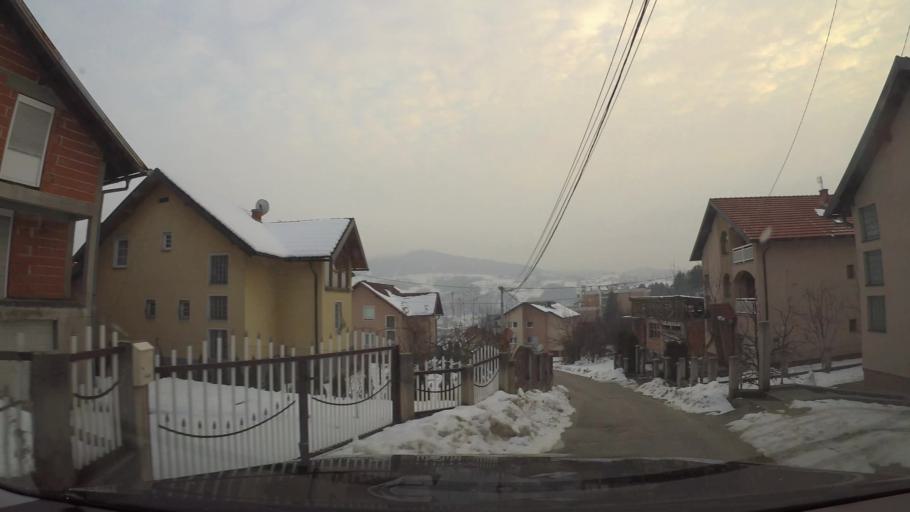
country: BA
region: Federation of Bosnia and Herzegovina
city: Vogosca
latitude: 43.9047
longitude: 18.3494
